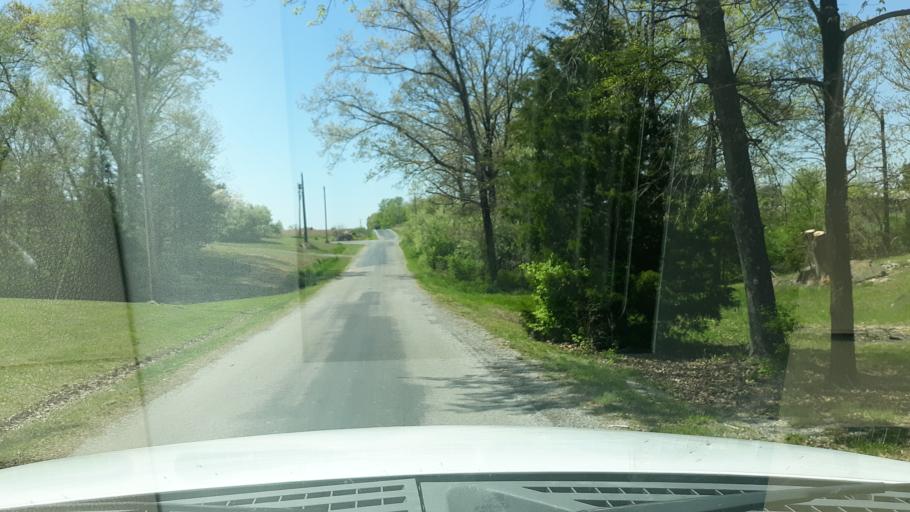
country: US
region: Illinois
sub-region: Saline County
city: Harrisburg
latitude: 37.8597
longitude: -88.6371
